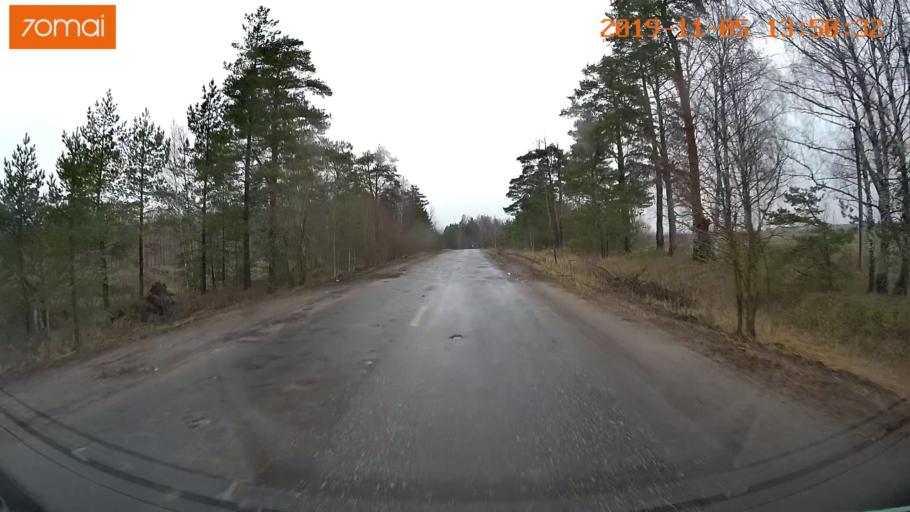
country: RU
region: Ivanovo
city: Kaminskiy
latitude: 57.0200
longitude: 41.4075
